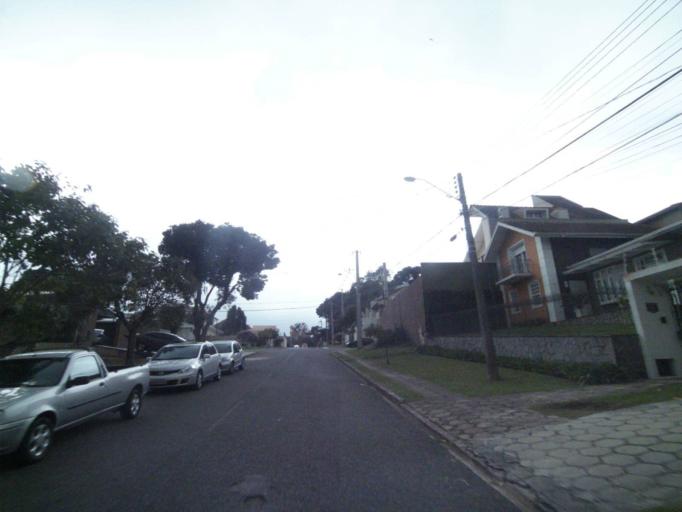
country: BR
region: Parana
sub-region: Curitiba
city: Curitiba
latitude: -25.4061
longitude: -49.2691
